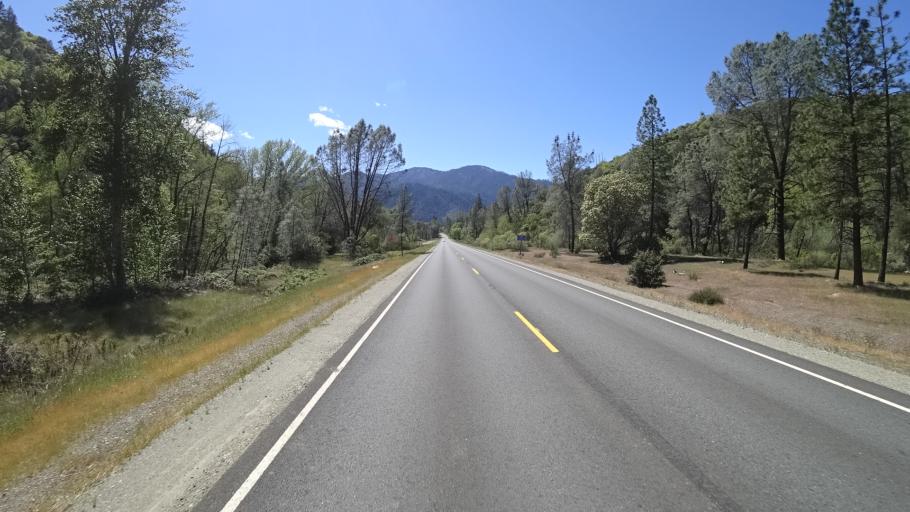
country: US
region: California
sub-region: Trinity County
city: Weaverville
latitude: 40.7312
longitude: -123.0284
